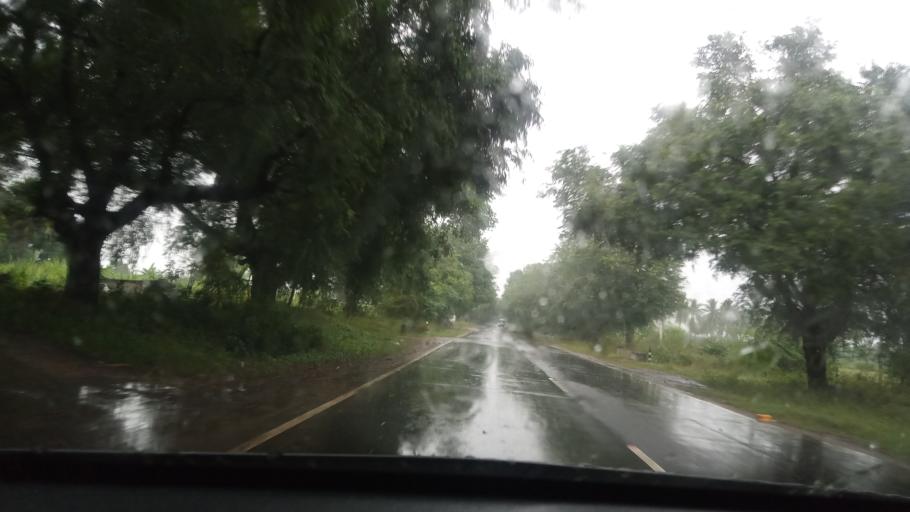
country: IN
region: Tamil Nadu
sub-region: Vellore
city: Kalavai
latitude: 12.8463
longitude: 79.3946
